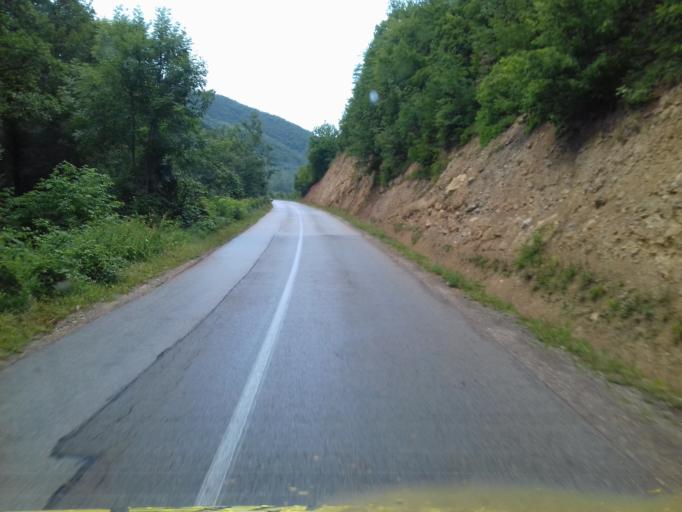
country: BA
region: Federation of Bosnia and Herzegovina
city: Visoko
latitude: 43.9563
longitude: 18.1557
